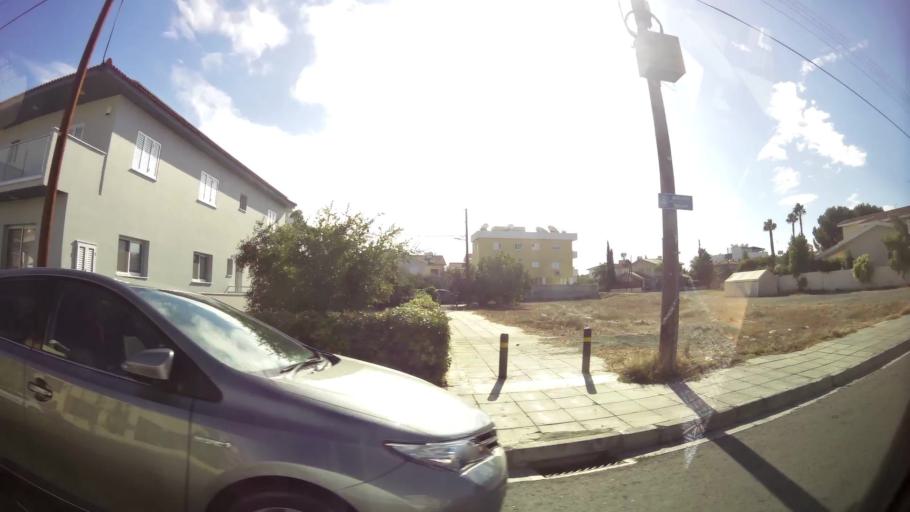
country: CY
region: Lefkosia
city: Nicosia
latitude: 35.1322
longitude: 33.3487
